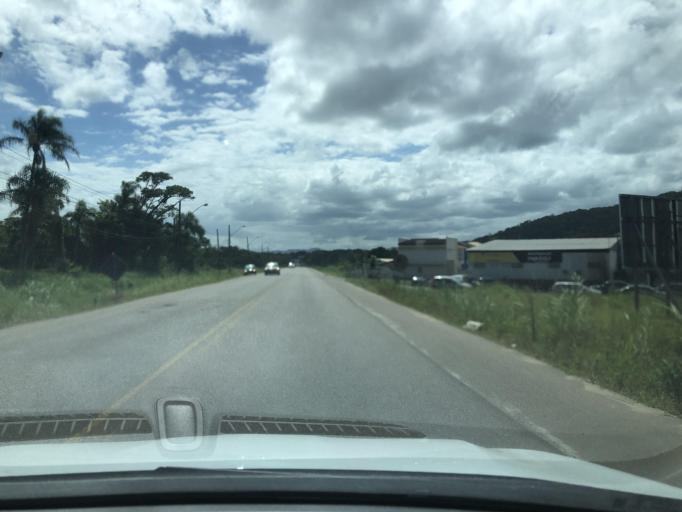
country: BR
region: Santa Catarina
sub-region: Sao Francisco Do Sul
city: Sao Francisco do Sul
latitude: -26.2062
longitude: -48.5303
